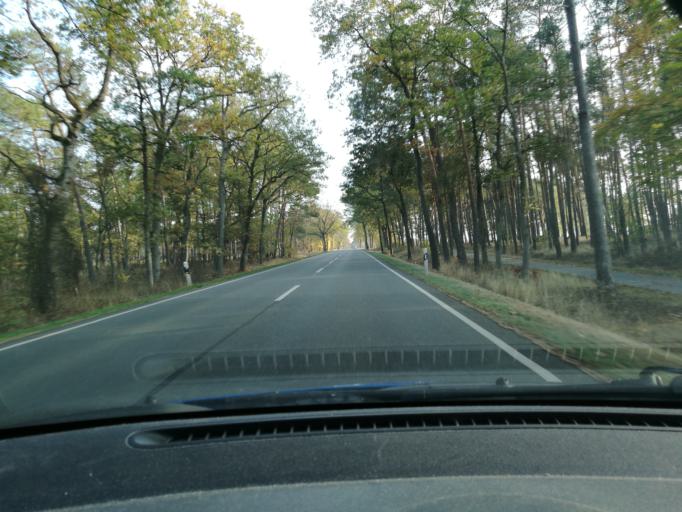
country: DE
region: Lower Saxony
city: Kusten
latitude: 52.9986
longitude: 11.1079
